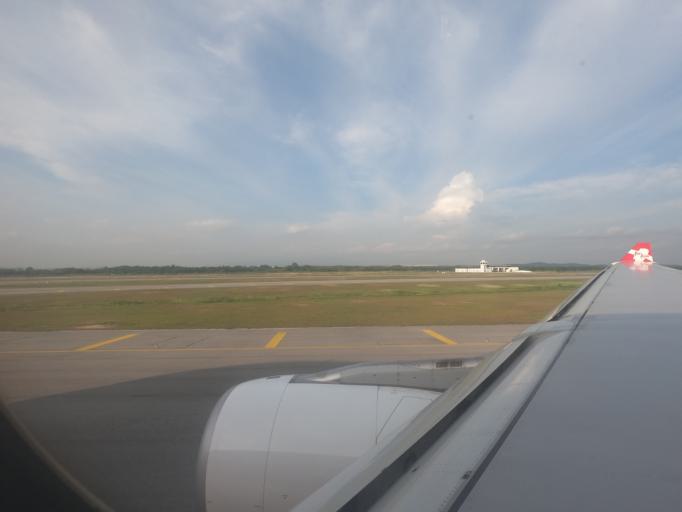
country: MY
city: Sungai Pelek New Village
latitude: 2.7259
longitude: 101.6863
